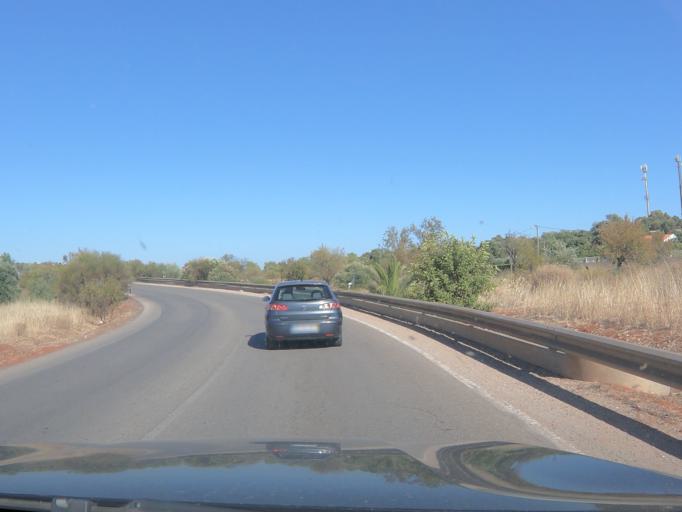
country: PT
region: Faro
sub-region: Loule
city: Almancil
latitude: 37.1028
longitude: -8.0557
